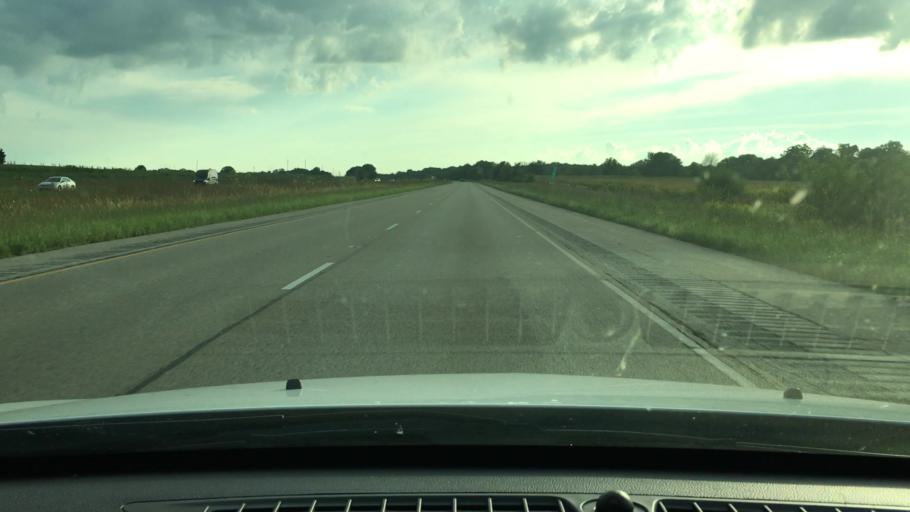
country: US
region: Illinois
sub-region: Logan County
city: Atlanta
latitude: 40.3492
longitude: -89.1240
